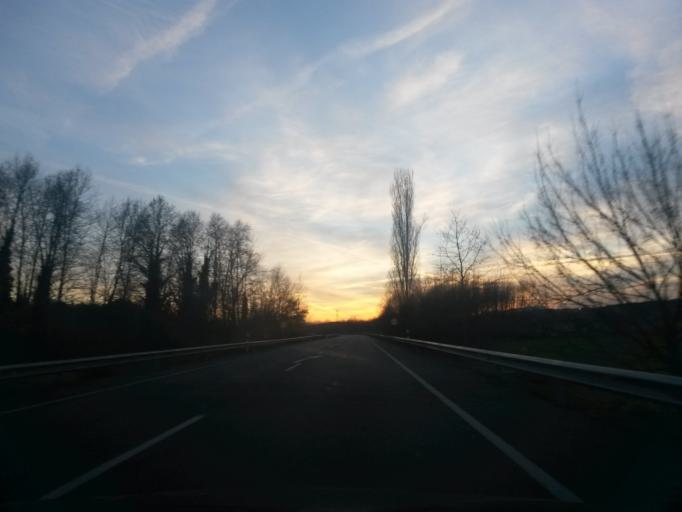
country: ES
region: Catalonia
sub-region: Provincia de Girona
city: Quart d'Onyar
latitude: 41.9504
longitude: 2.8296
